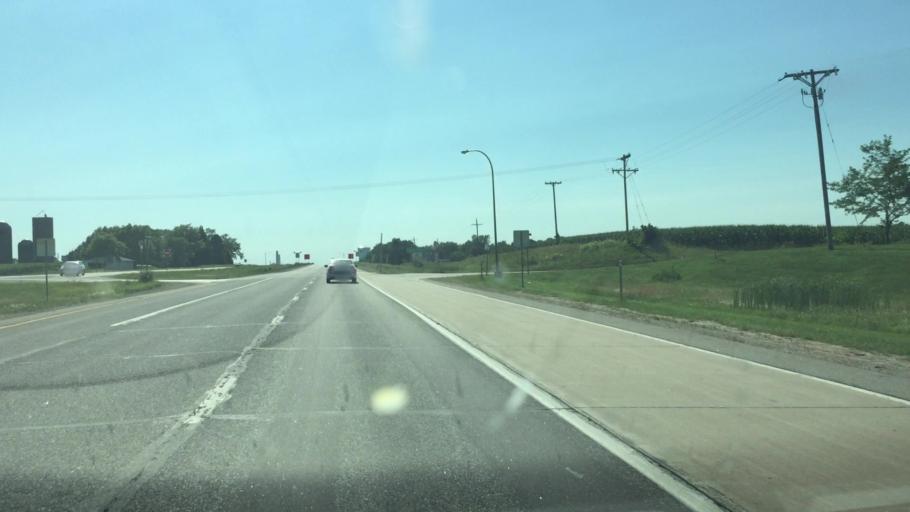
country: US
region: Iowa
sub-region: Linn County
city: Ely
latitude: 41.9264
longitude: -91.6174
